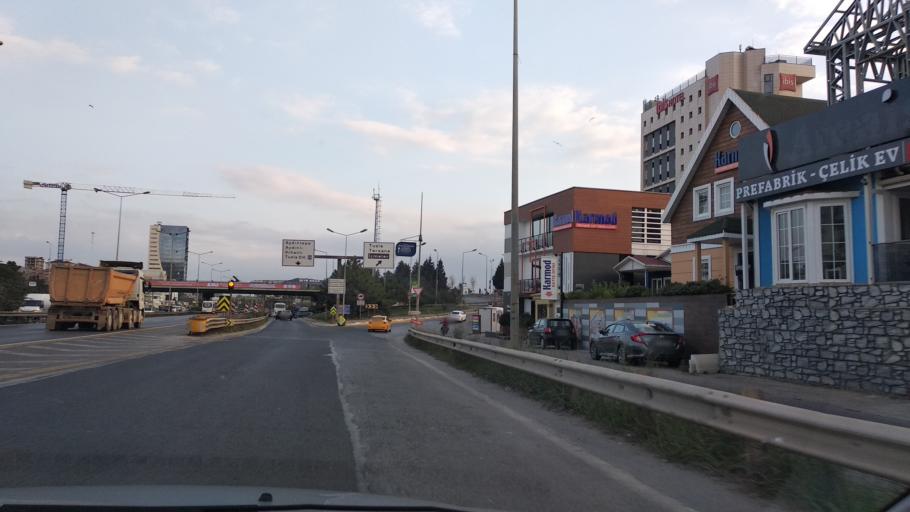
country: TR
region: Istanbul
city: Icmeler
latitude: 40.8506
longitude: 29.2965
